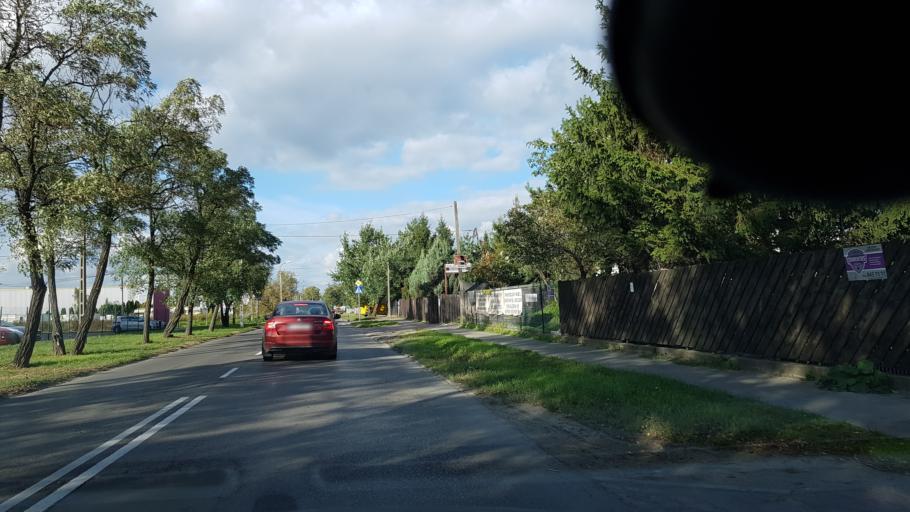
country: PL
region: Masovian Voivodeship
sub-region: Warszawa
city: Targowek
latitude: 52.3087
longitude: 21.0300
